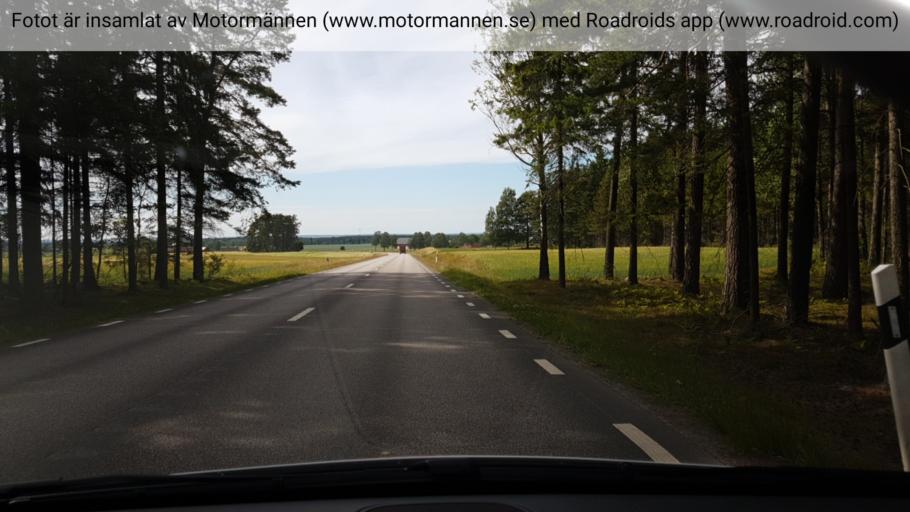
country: SE
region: Vaestra Goetaland
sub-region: Tibro Kommun
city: Tibro
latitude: 58.3445
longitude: 14.1529
